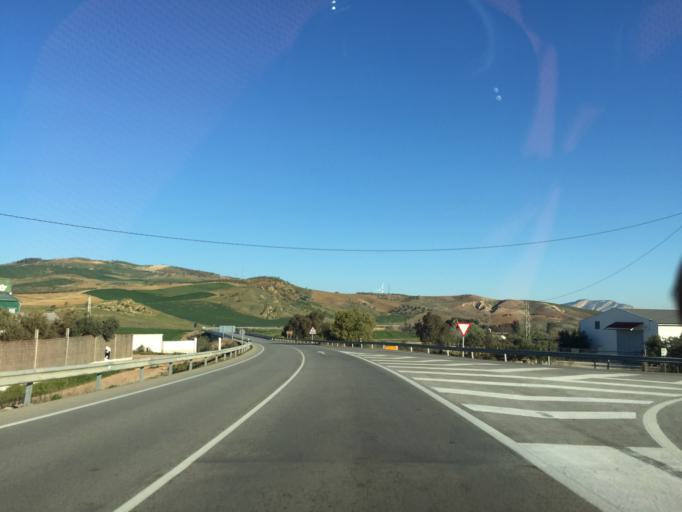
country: ES
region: Andalusia
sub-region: Provincia de Malaga
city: Ardales
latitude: 36.8873
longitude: -4.8448
